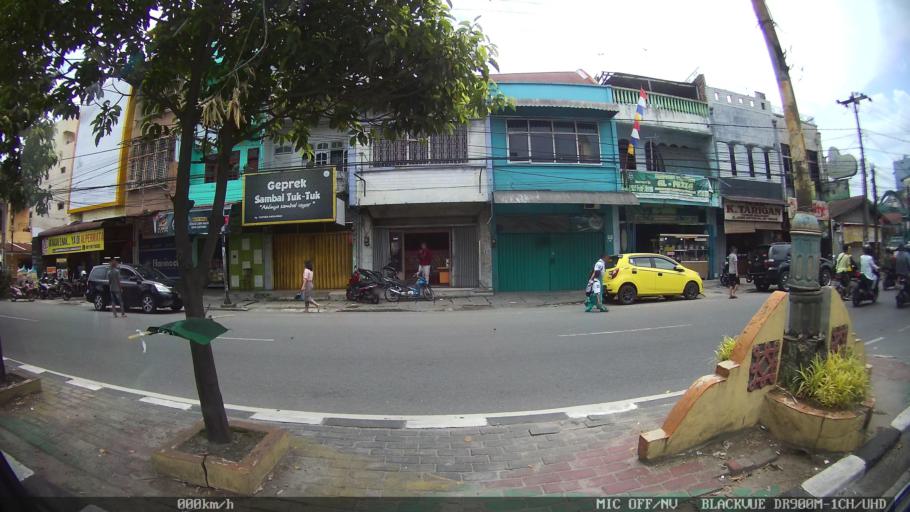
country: ID
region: North Sumatra
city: Medan
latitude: 3.5654
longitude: 98.6620
